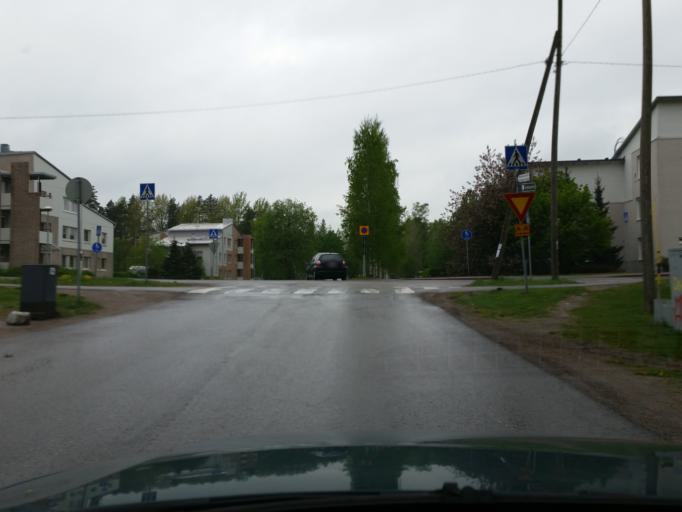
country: FI
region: Uusimaa
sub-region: Helsinki
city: Kilo
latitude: 60.2309
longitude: 24.8143
